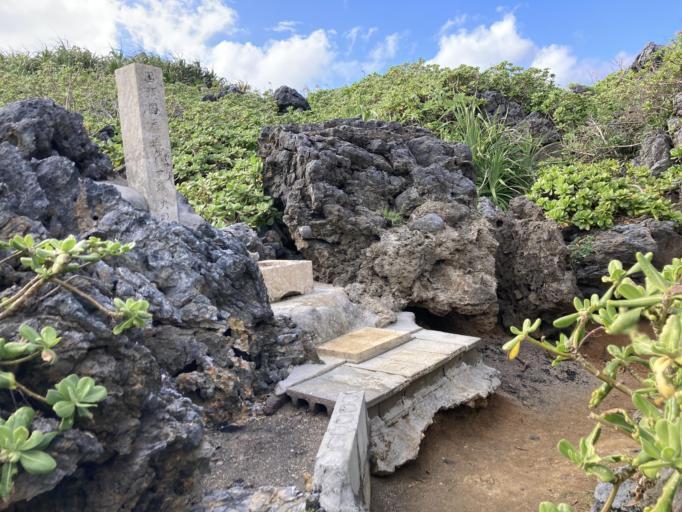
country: JP
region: Okinawa
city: Nago
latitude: 26.8738
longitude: 128.2634
